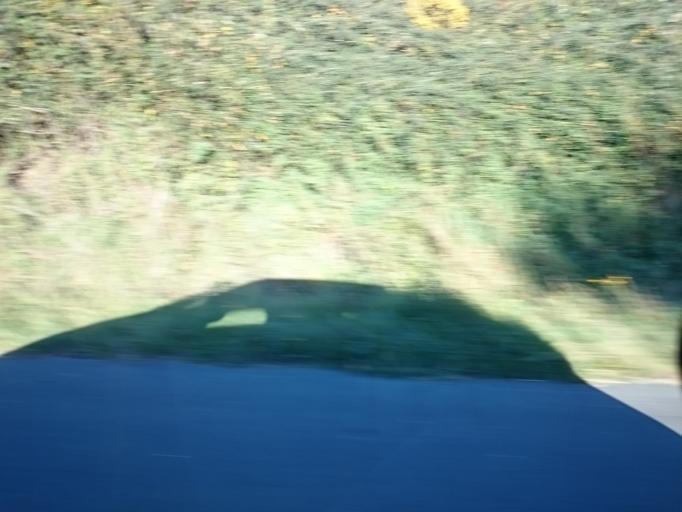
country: FR
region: Brittany
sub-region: Departement d'Ille-et-Vilaine
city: Quedillac
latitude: 48.2619
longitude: -2.1448
